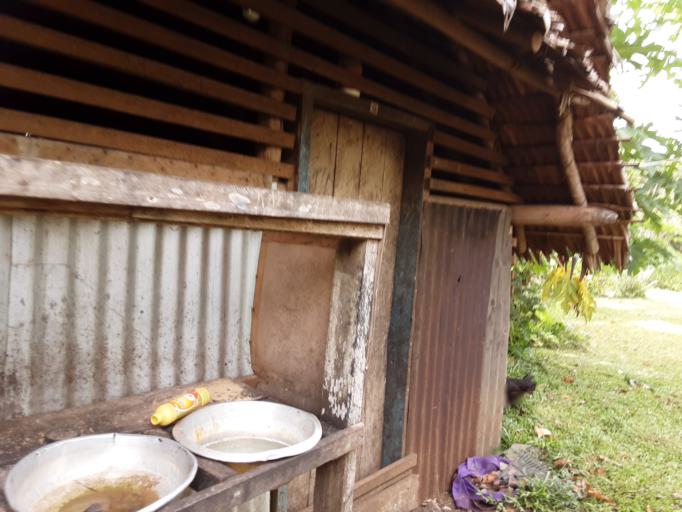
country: VU
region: Sanma
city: Luganville
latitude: -15.5804
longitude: 167.0018
